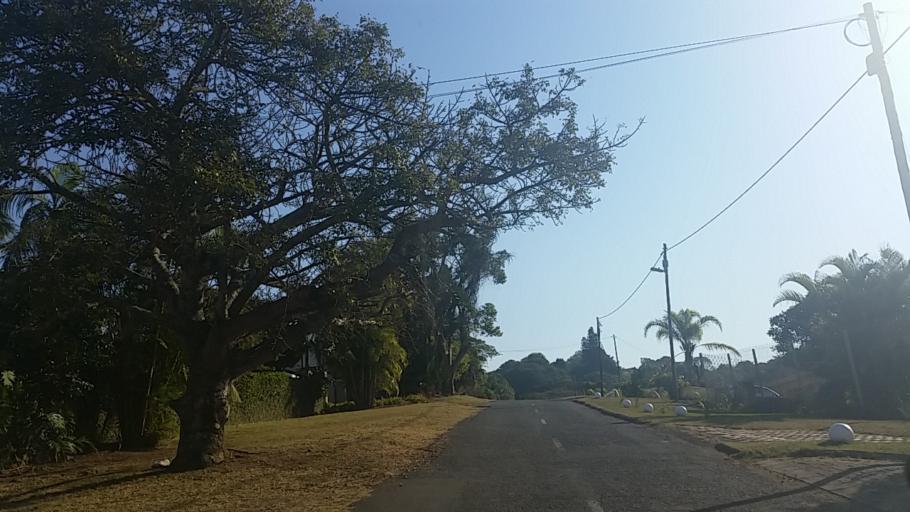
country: ZA
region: KwaZulu-Natal
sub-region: eThekwini Metropolitan Municipality
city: Berea
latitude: -29.8453
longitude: 30.9163
